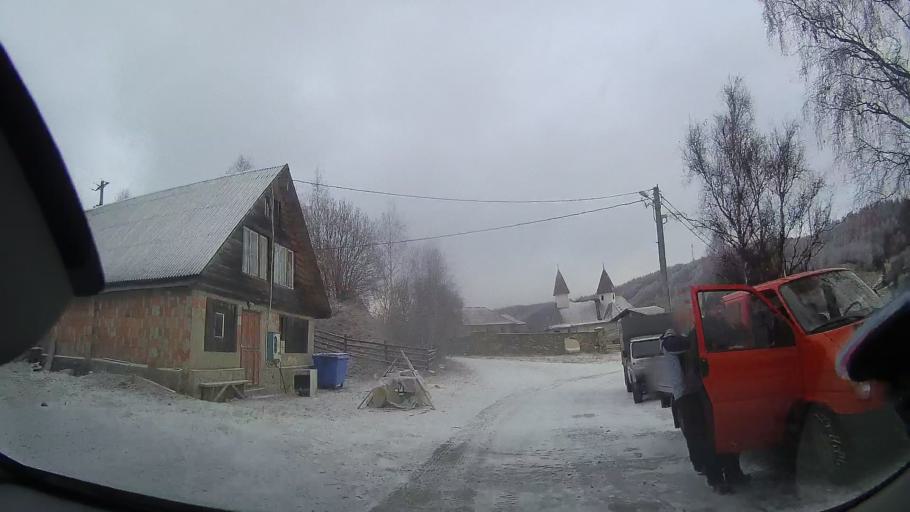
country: RO
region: Cluj
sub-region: Comuna Valea Ierii
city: Valea Ierii
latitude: 46.6632
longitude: 23.3332
